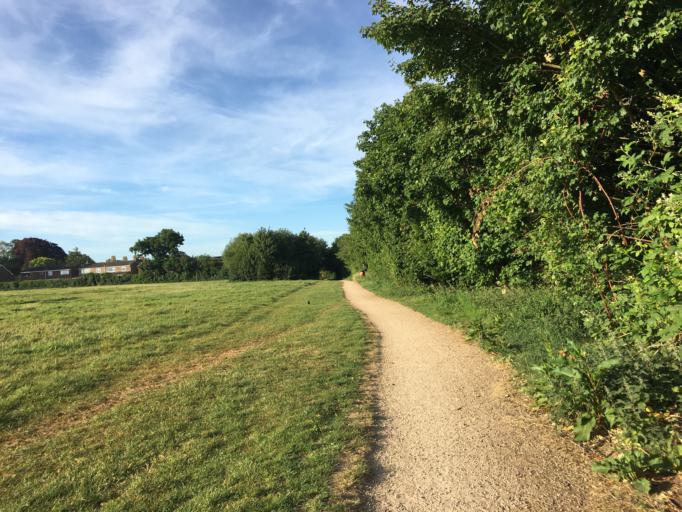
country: GB
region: England
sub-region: Warwickshire
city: Rugby
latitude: 52.3611
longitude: -1.2258
